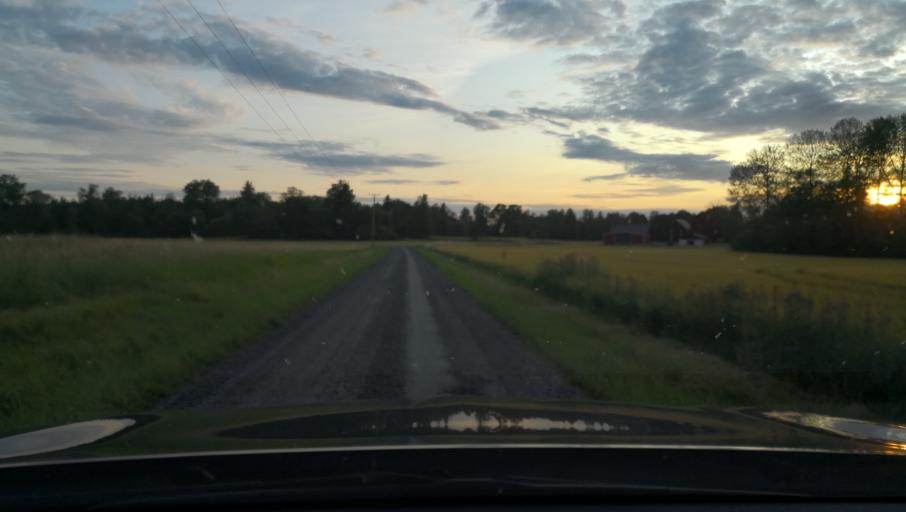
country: SE
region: Uppsala
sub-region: Osthammars Kommun
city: Bjorklinge
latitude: 60.0541
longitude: 17.6294
